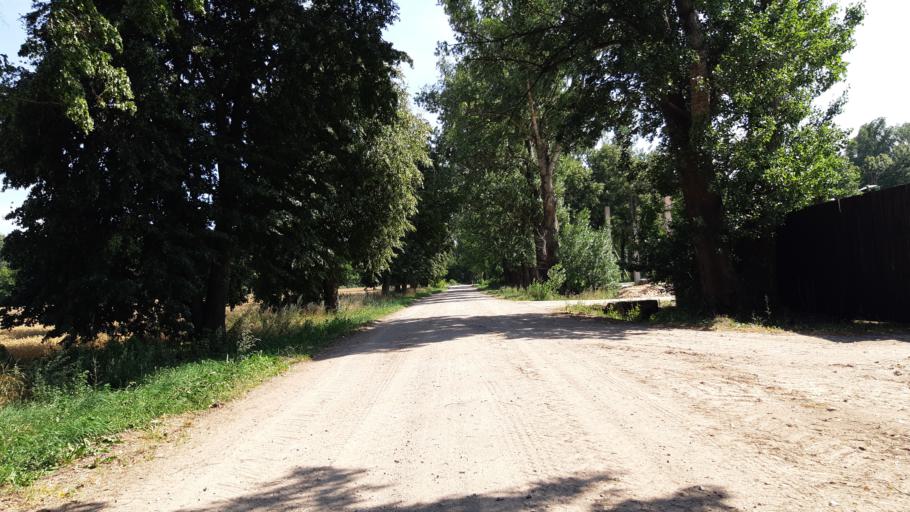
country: LT
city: Virbalis
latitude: 54.6371
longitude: 22.8238
